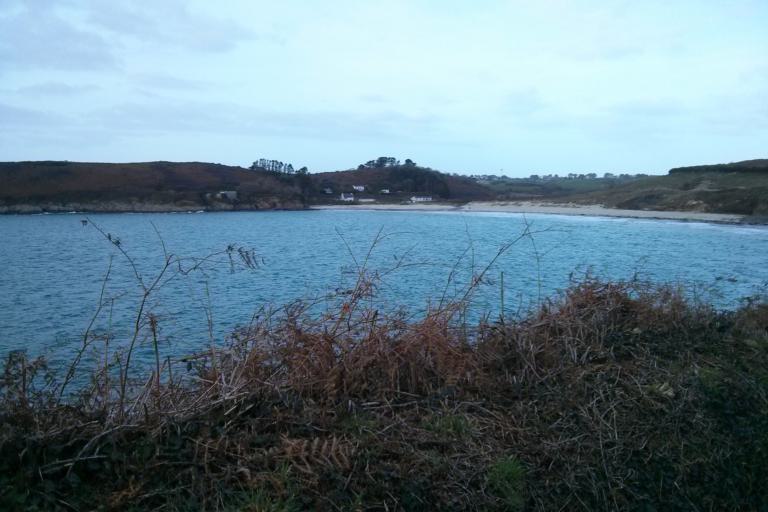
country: FR
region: Brittany
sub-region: Departement du Finistere
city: Le Conquet
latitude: 48.4015
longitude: -4.7747
